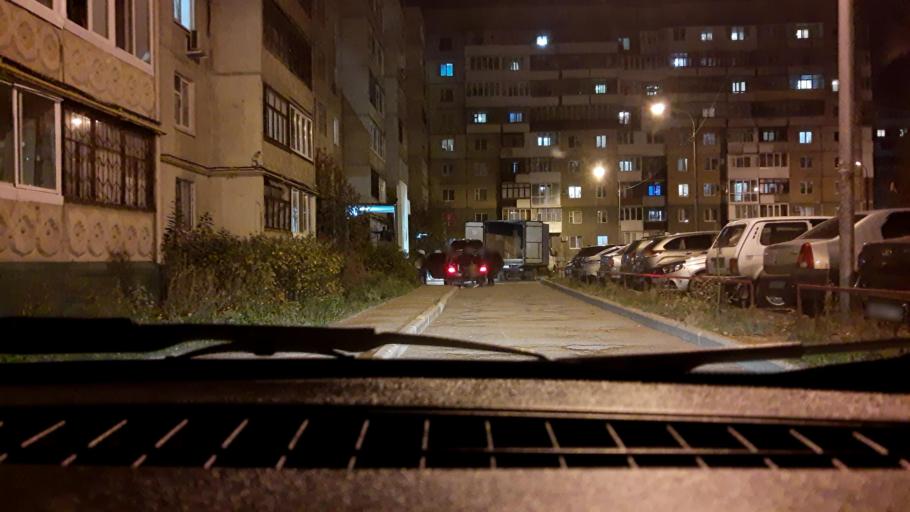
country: RU
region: Bashkortostan
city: Ufa
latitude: 54.7811
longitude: 56.1091
